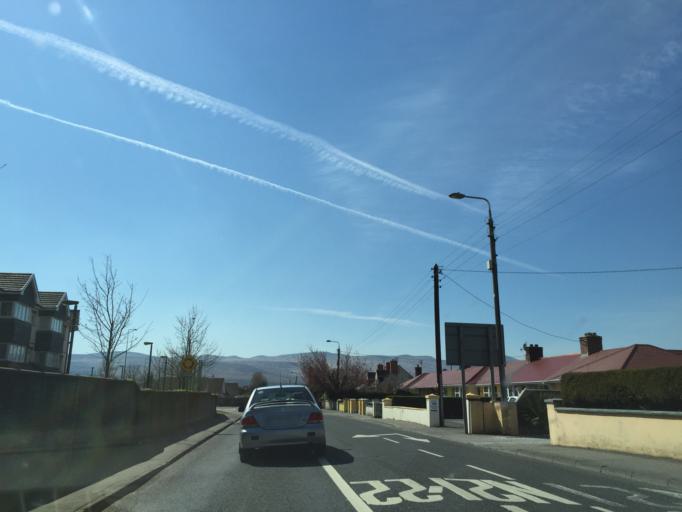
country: IE
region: Munster
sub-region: Ciarrai
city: Tralee
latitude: 52.2643
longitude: -9.6811
